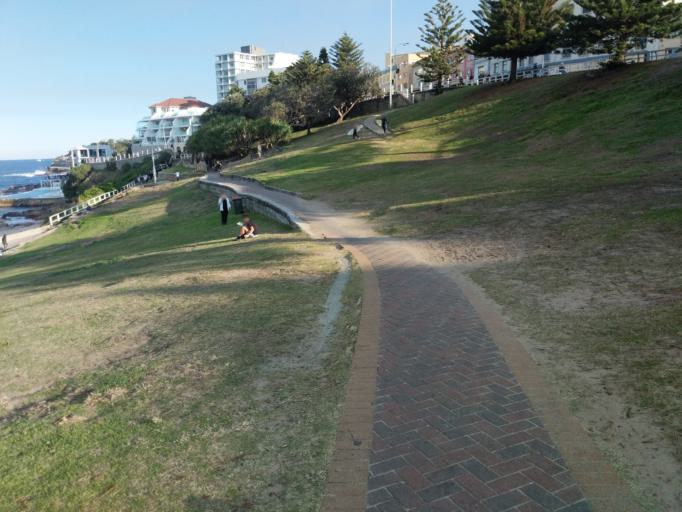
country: AU
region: New South Wales
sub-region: Waverley
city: Bondi Beach
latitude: -33.8929
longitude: 151.2734
